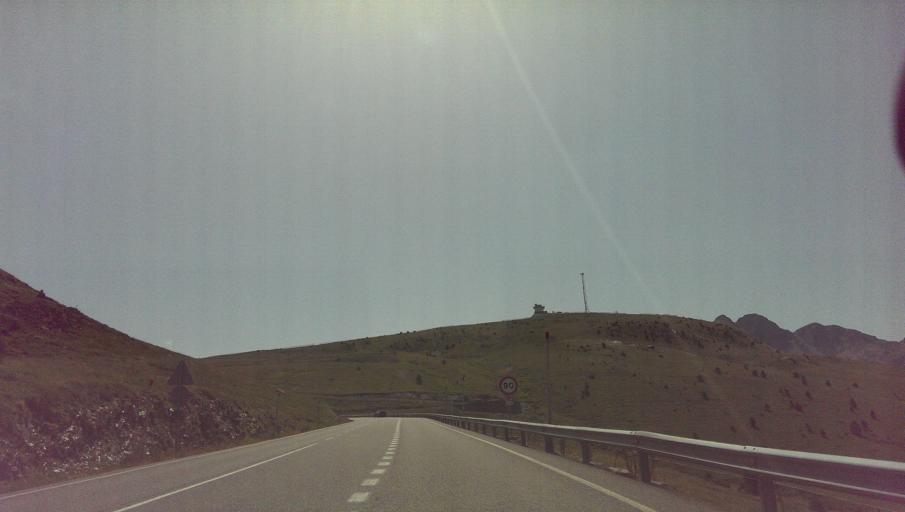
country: AD
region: Encamp
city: Pas de la Casa
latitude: 42.5430
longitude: 1.7089
